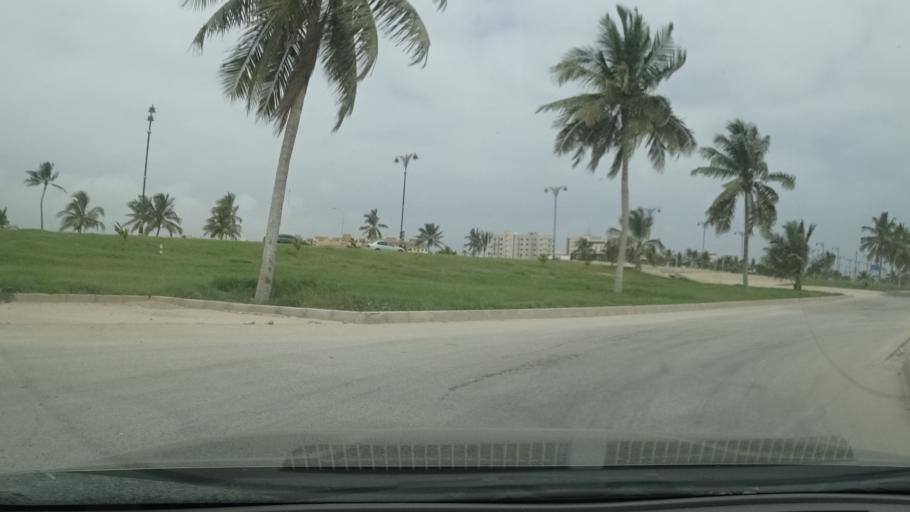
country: OM
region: Zufar
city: Salalah
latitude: 17.0260
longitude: 54.0576
